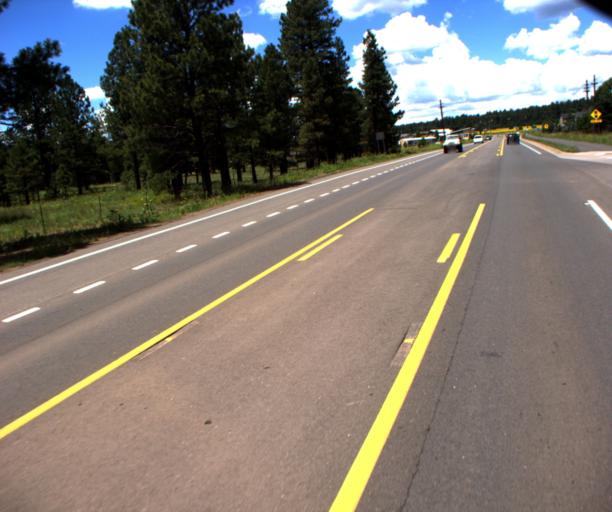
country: US
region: Arizona
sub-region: Coconino County
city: Flagstaff
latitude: 35.2359
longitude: -111.6659
